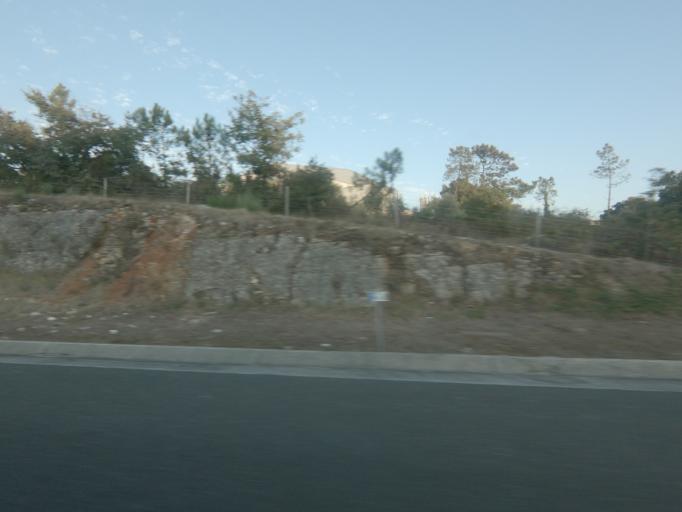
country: PT
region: Leiria
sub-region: Leiria
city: Santa Catarina da Serra
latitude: 39.6613
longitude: -8.6922
